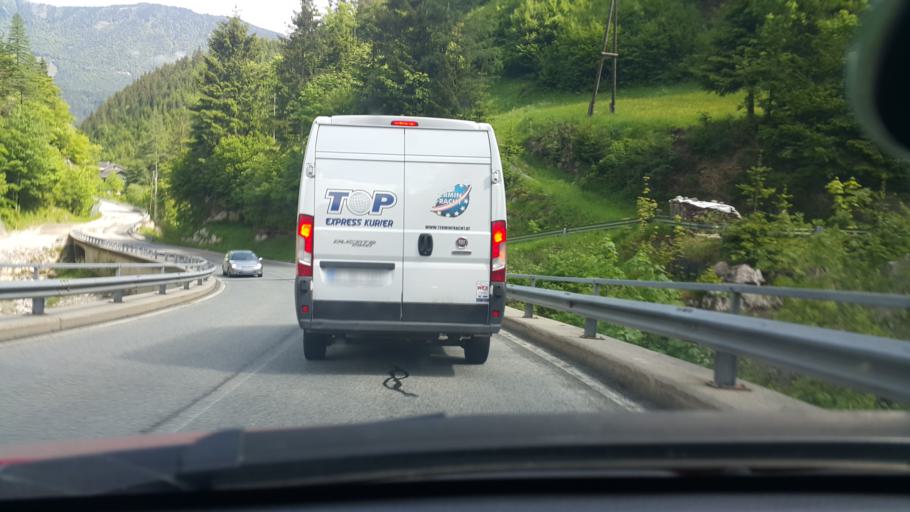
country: AT
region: Carinthia
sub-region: Politischer Bezirk Klagenfurt Land
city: Ferlach
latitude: 46.4569
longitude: 14.2591
